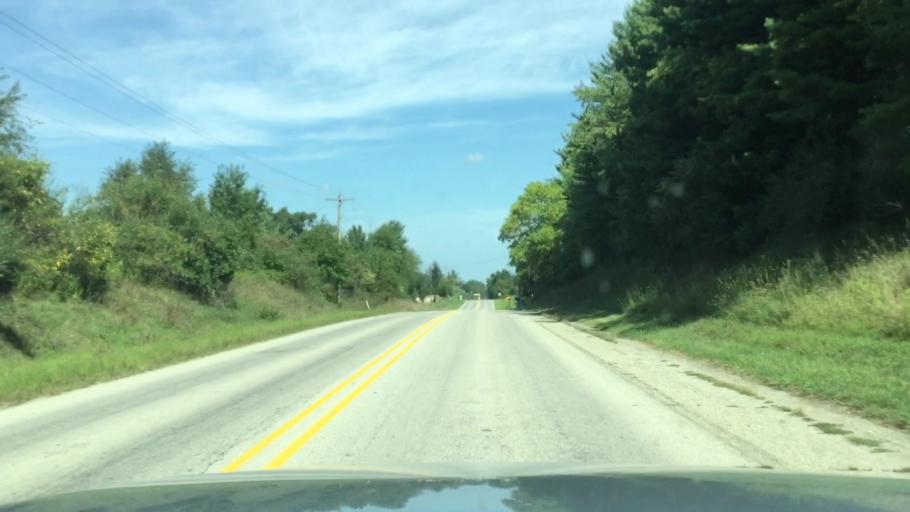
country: US
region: Michigan
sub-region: Lenawee County
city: Manitou Beach-Devils Lake
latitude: 42.0139
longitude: -84.2762
